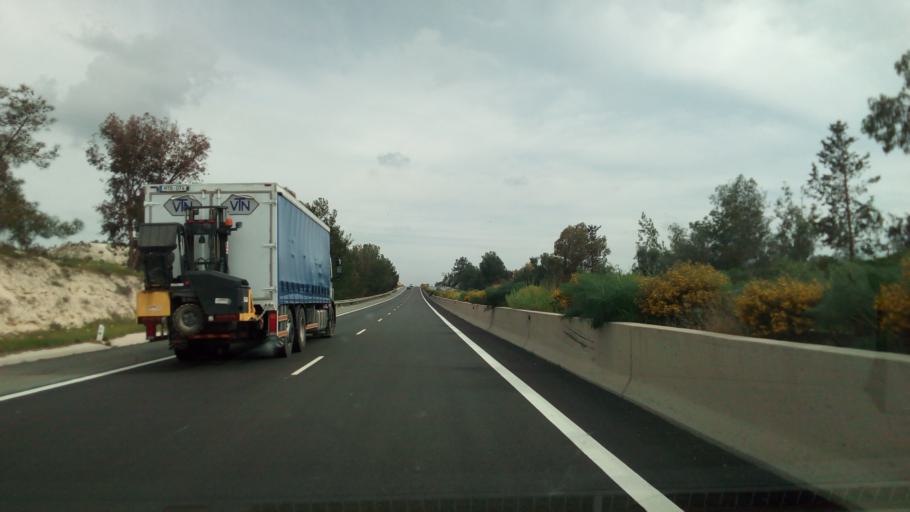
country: CY
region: Larnaka
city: Aradippou
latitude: 34.9727
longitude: 33.5420
